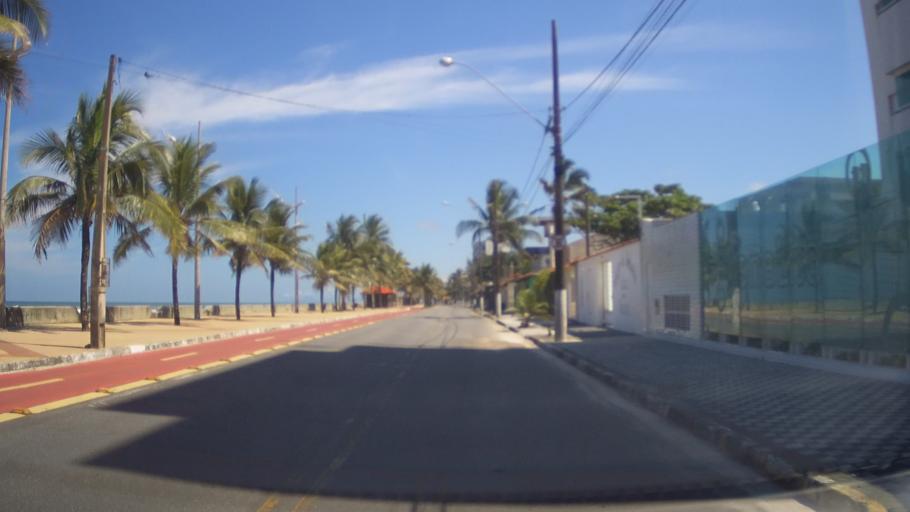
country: BR
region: Sao Paulo
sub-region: Mongagua
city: Mongagua
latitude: -24.1123
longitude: -46.6520
